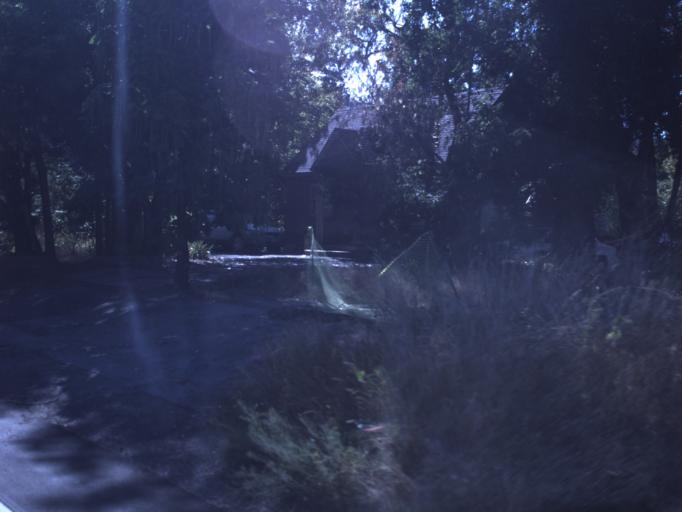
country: US
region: Utah
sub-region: Salt Lake County
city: Holladay
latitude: 40.6742
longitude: -111.8342
